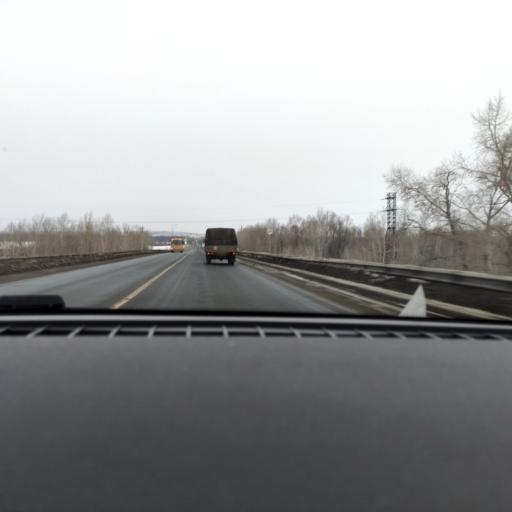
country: RU
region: Samara
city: Kinel'
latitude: 53.1886
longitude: 50.5154
